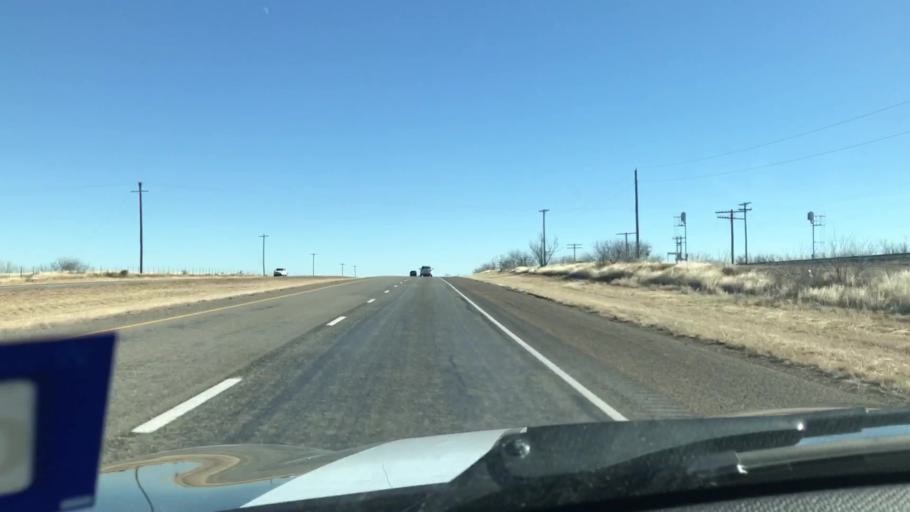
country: US
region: Texas
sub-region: Garza County
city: Post
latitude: 33.1354
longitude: -101.3083
